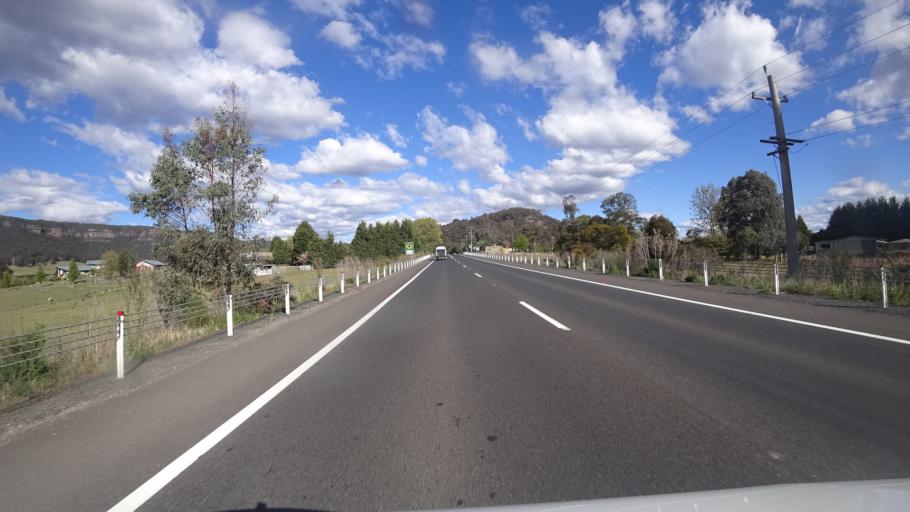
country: AU
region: New South Wales
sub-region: Lithgow
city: Bowenfels
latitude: -33.5673
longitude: 150.2043
